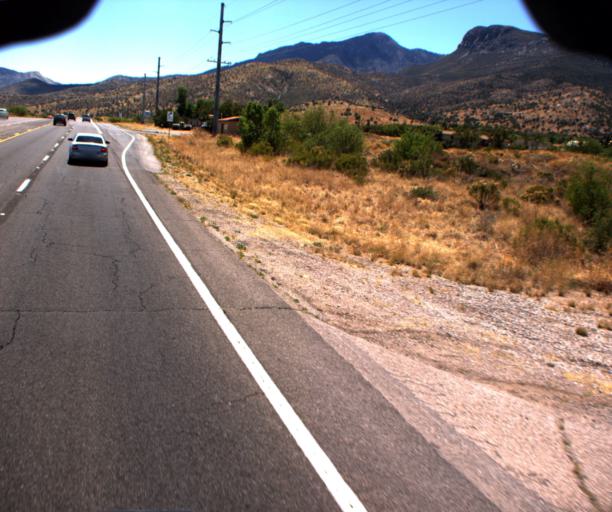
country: US
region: Arizona
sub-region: Cochise County
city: Sierra Vista Southeast
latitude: 31.4552
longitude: -110.2575
